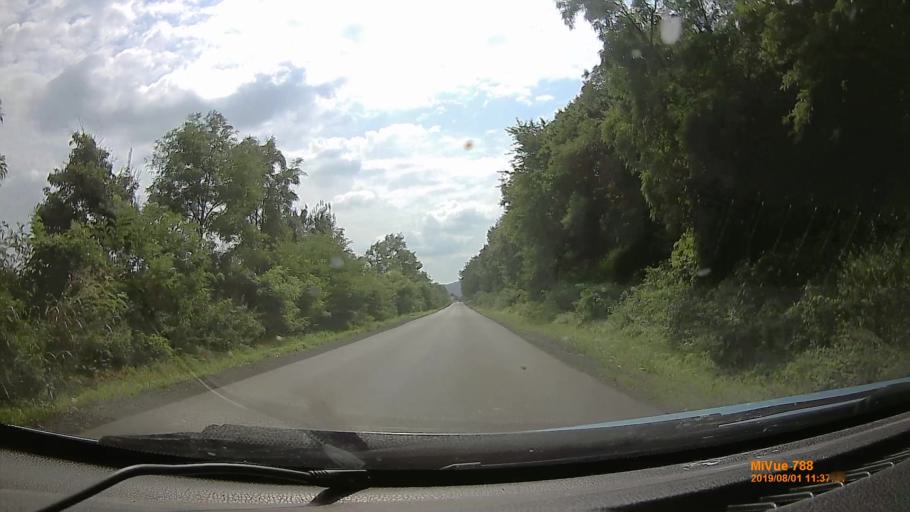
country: HU
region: Baranya
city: Villany
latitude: 45.9076
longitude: 18.3823
